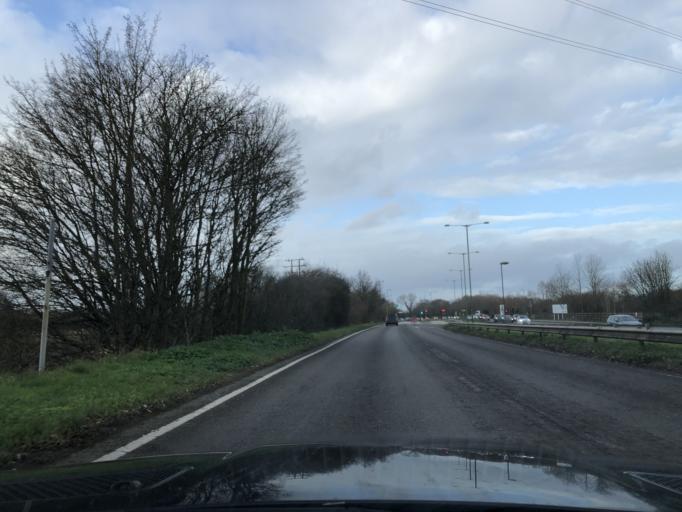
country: GB
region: England
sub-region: Surrey
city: Frimley
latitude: 51.3228
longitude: -0.7647
